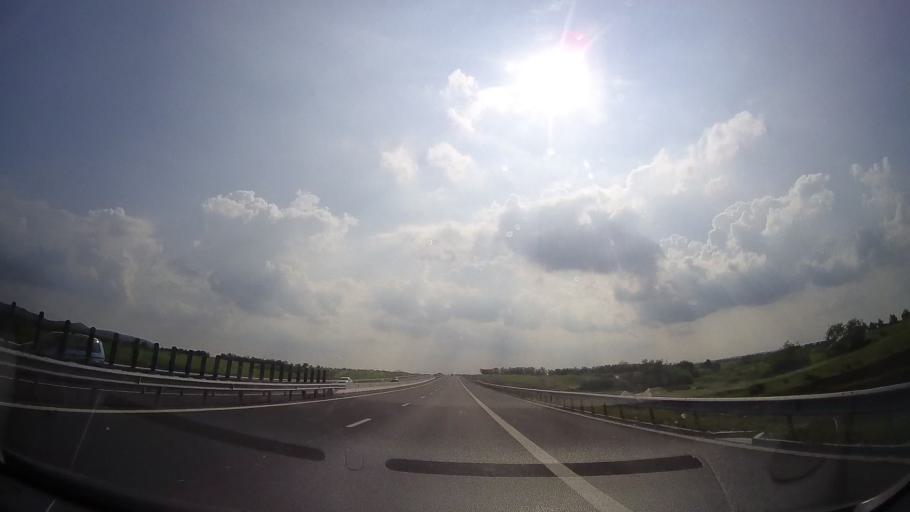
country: RO
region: Timis
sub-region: Comuna Faget
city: Faget
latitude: 45.8188
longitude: 22.1578
